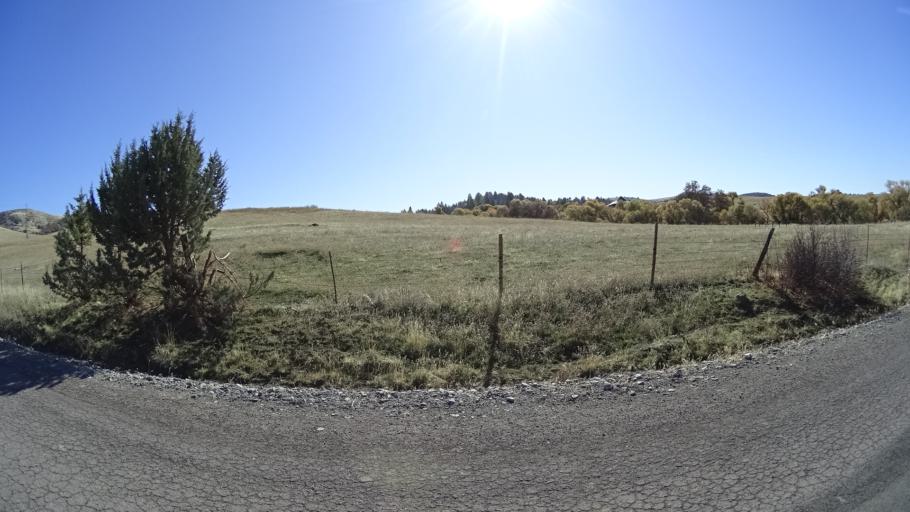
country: US
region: California
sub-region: Siskiyou County
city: Montague
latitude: 41.8153
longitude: -122.3740
